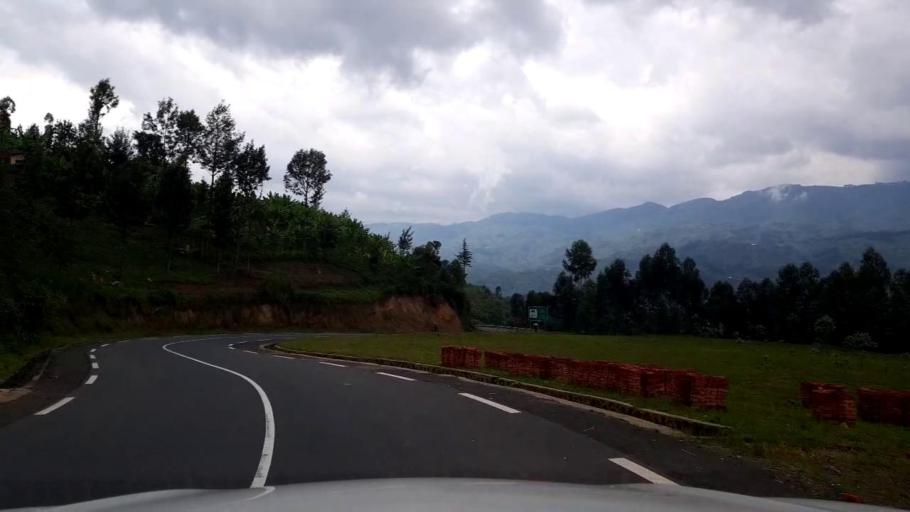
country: RW
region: Western Province
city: Kibuye
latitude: -1.9050
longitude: 29.3580
